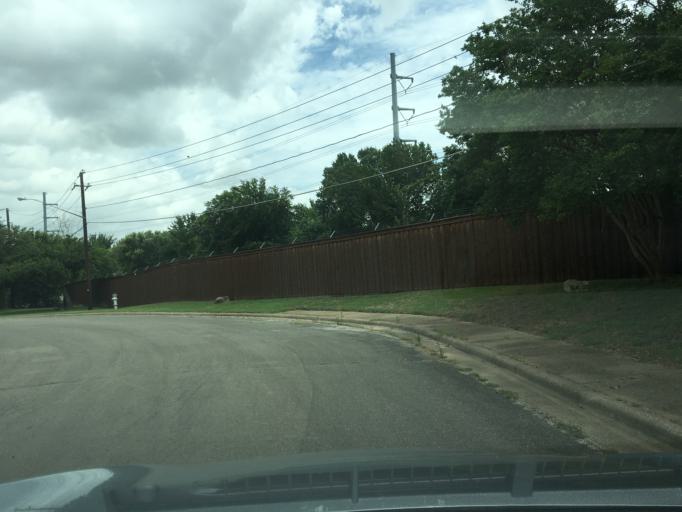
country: US
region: Texas
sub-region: Dallas County
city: Richardson
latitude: 32.9162
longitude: -96.7110
